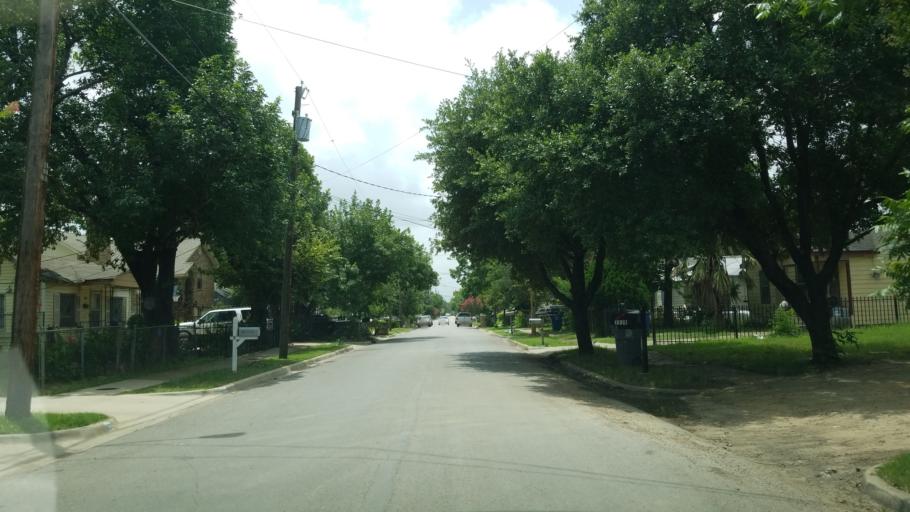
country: US
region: Texas
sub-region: Dallas County
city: Irving
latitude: 32.7903
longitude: -96.9014
